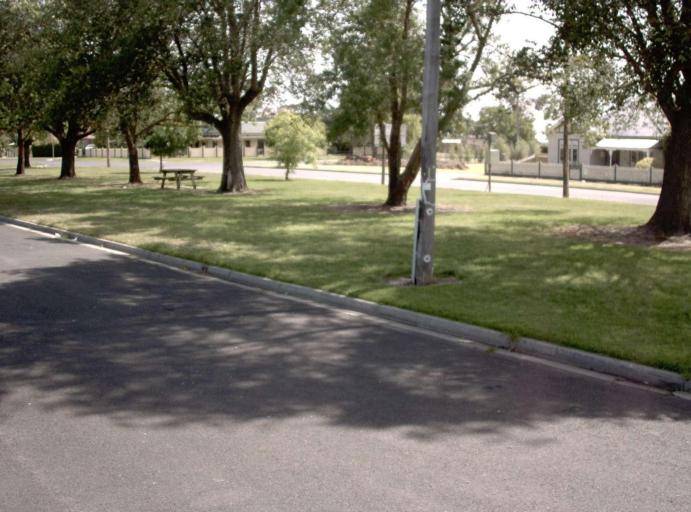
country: AU
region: Victoria
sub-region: Wellington
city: Heyfield
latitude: -38.1521
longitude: 146.7897
